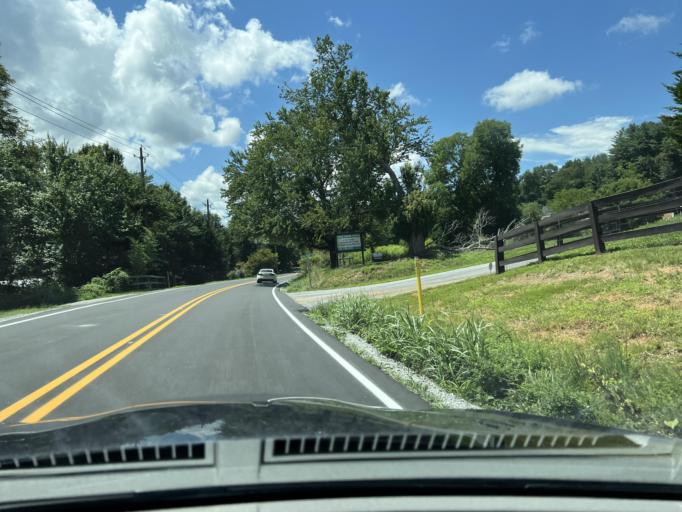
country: US
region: North Carolina
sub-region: Buncombe County
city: Fairview
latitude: 35.5030
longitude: -82.4206
